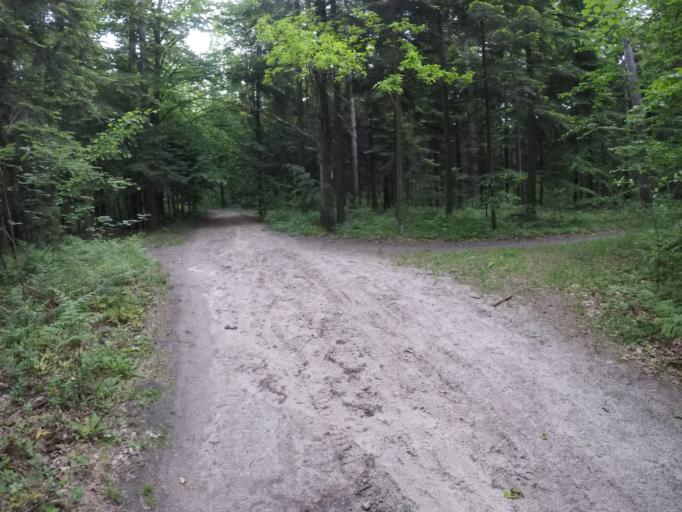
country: PL
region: Swietokrzyskie
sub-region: Powiat kielecki
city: Kielce
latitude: 50.8365
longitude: 20.6041
